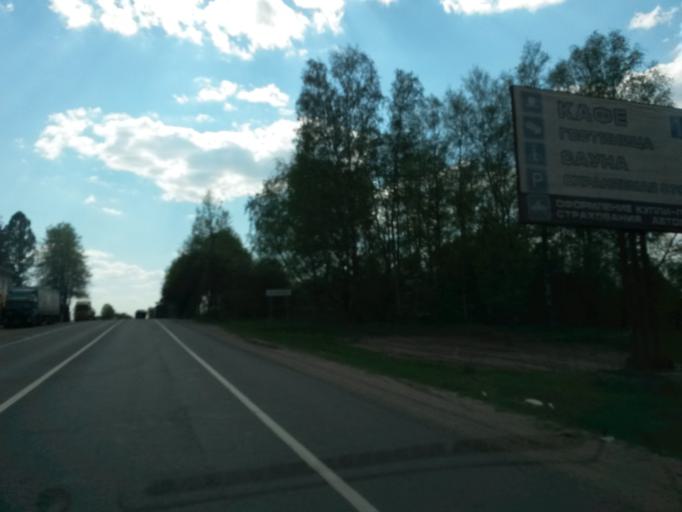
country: RU
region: Jaroslavl
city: Petrovsk
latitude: 56.8999
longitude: 39.1105
